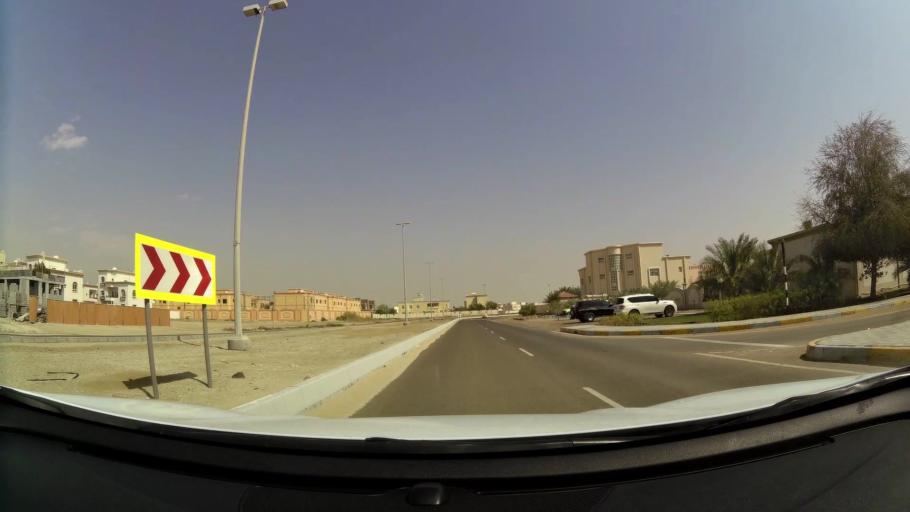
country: AE
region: Abu Dhabi
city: Abu Dhabi
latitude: 24.3414
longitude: 54.5605
